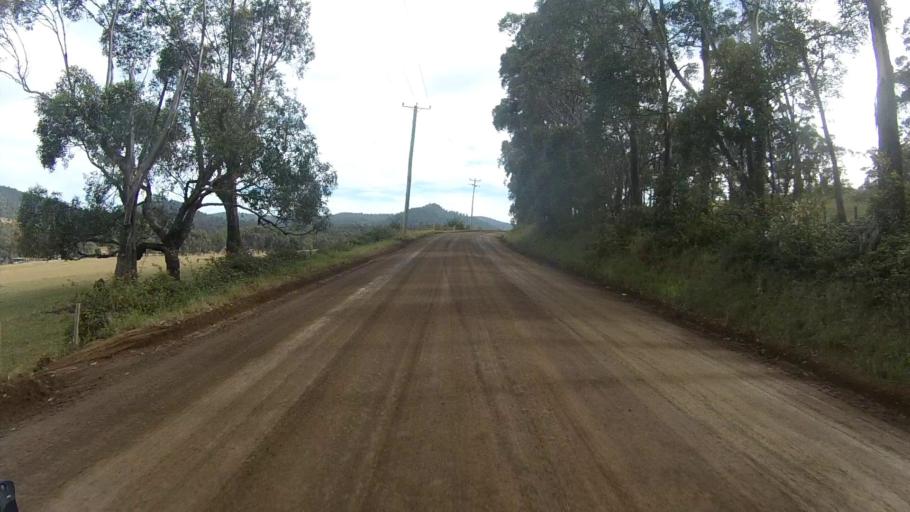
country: AU
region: Tasmania
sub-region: Sorell
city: Sorell
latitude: -42.7843
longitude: 147.8079
